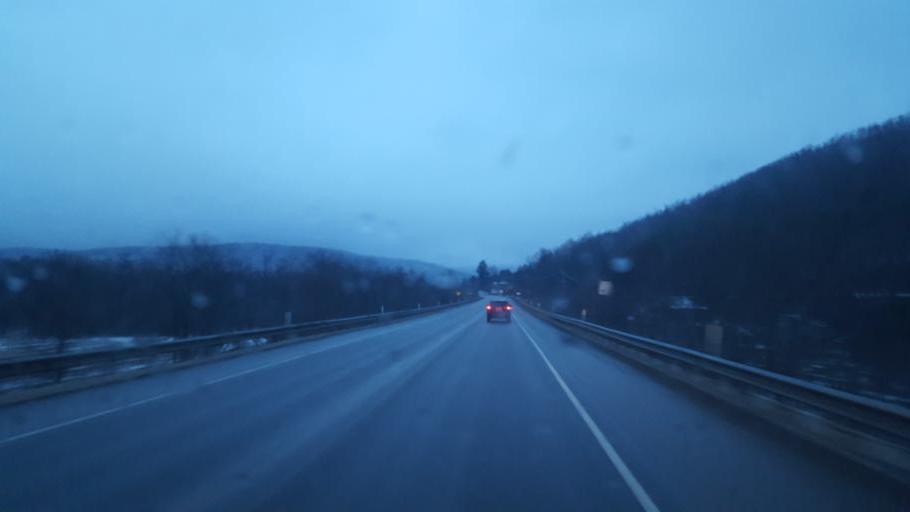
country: US
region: Pennsylvania
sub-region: McKean County
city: Port Allegany
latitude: 41.8018
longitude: -78.2667
